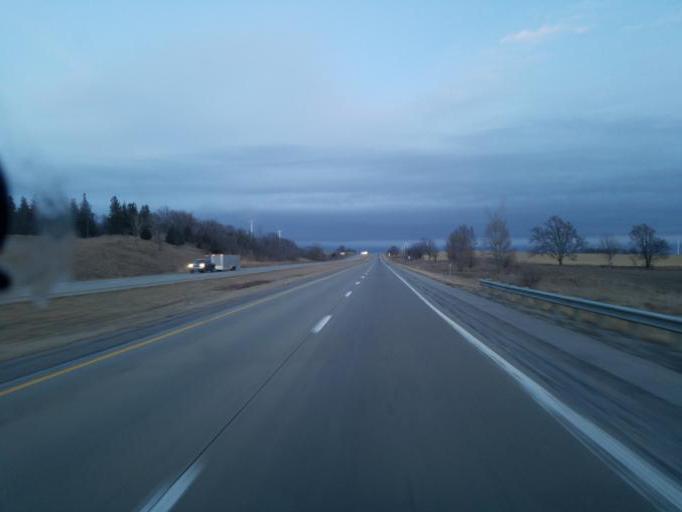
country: US
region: Iowa
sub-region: Pottawattamie County
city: Avoca
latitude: 41.4972
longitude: -95.2154
